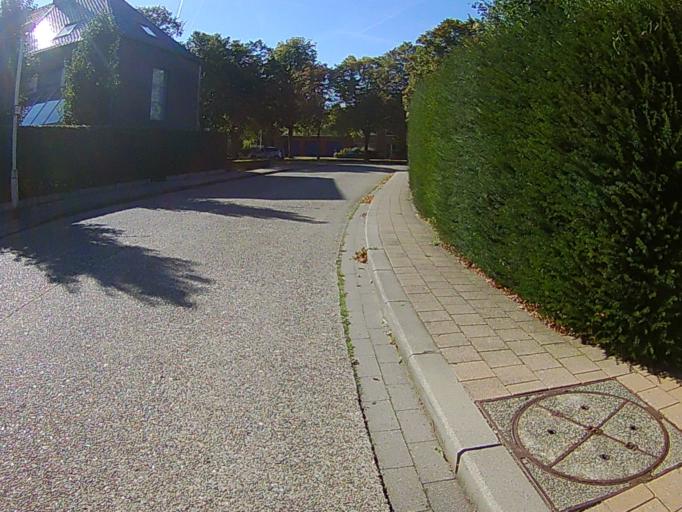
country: BE
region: Flanders
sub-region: Provincie Antwerpen
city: Kapellen
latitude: 51.3094
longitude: 4.4187
